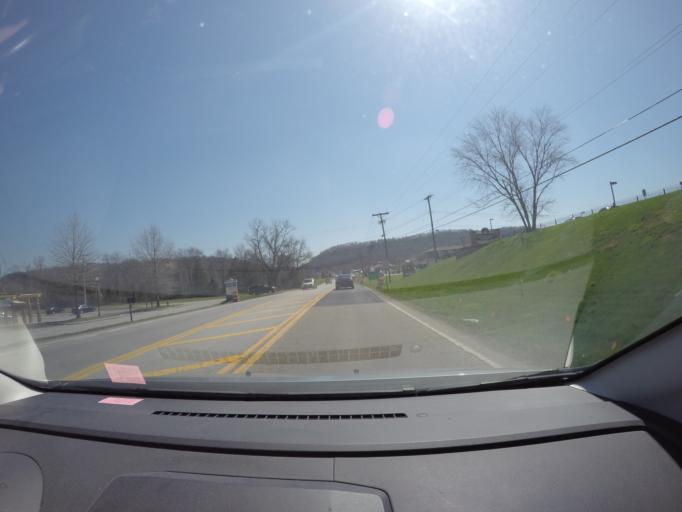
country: US
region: Tennessee
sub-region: Hamilton County
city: Collegedale
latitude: 35.0625
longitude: -85.0731
